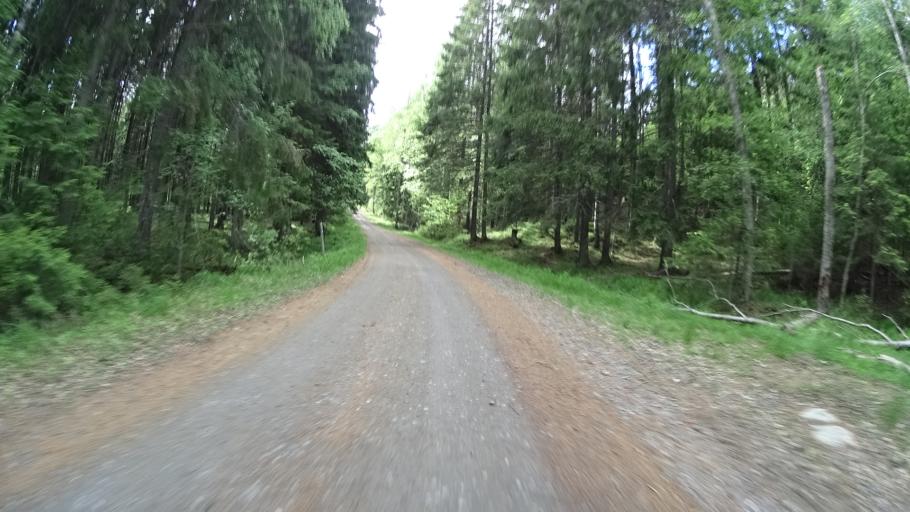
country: FI
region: Varsinais-Suomi
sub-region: Salo
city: Kisko
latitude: 60.1806
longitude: 23.5365
